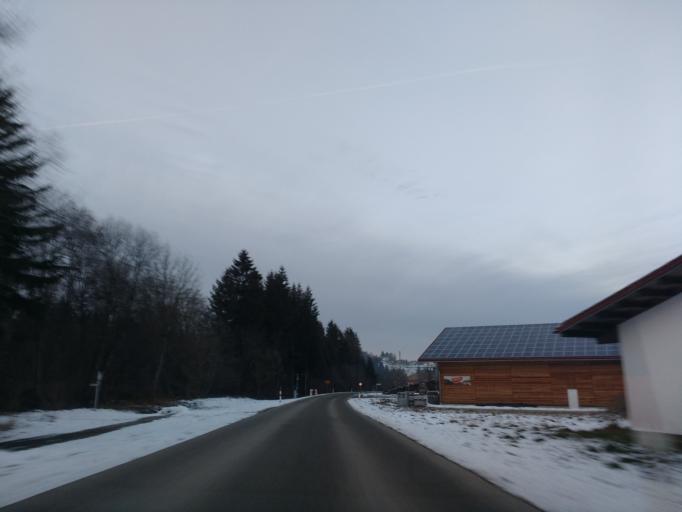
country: DE
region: Bavaria
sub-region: Swabia
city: Halblech
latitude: 47.6372
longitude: 10.8174
